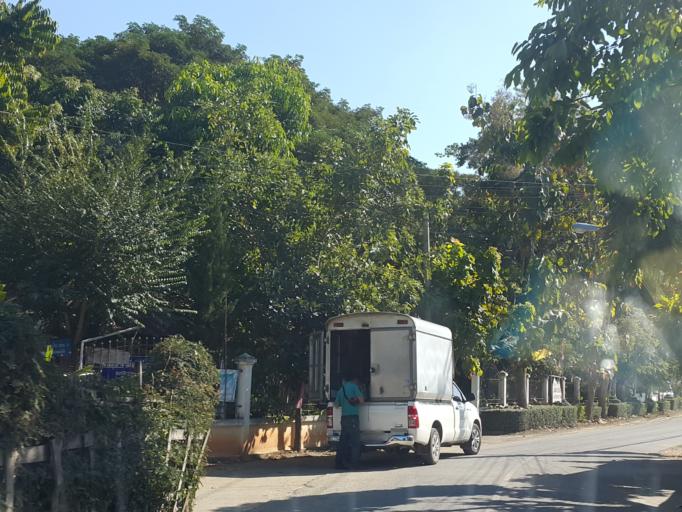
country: TH
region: Chiang Mai
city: San Sai
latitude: 18.8799
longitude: 99.0013
